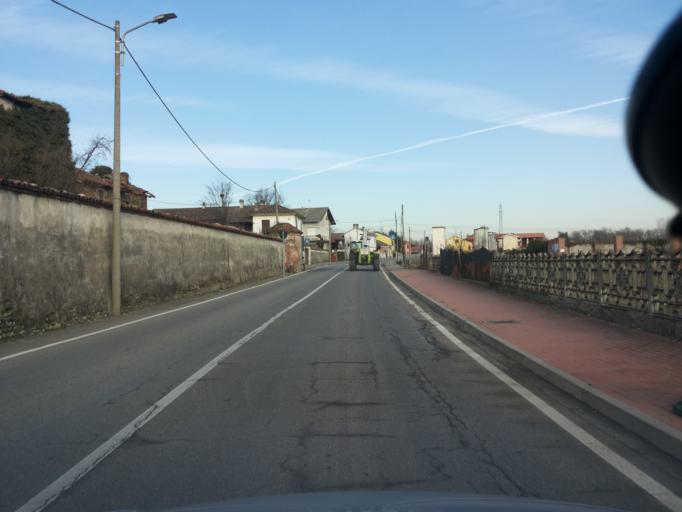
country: IT
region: Piedmont
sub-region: Provincia di Vercelli
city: Greggio
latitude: 45.4526
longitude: 8.3851
